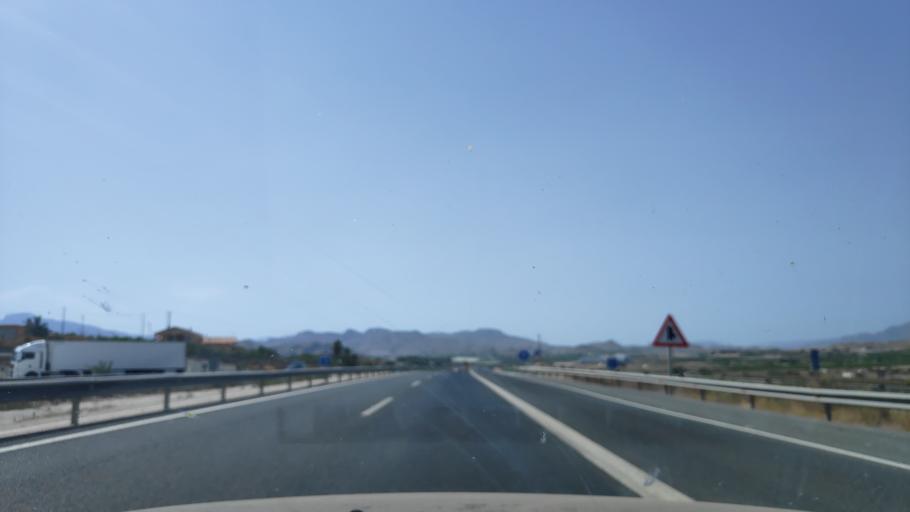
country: ES
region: Murcia
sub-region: Murcia
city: Lorqui
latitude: 38.1239
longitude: -1.2536
